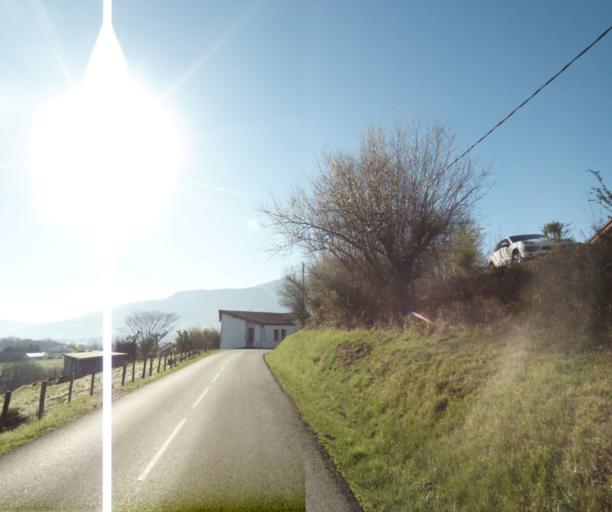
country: FR
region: Aquitaine
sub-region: Departement des Pyrenees-Atlantiques
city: Ciboure
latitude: 43.3505
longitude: -1.6683
